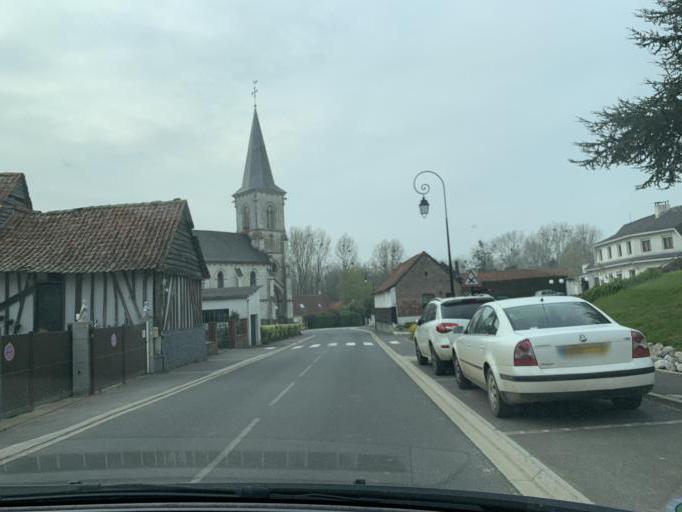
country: FR
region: Nord-Pas-de-Calais
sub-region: Departement du Pas-de-Calais
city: Montreuil
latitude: 50.4989
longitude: 1.7925
